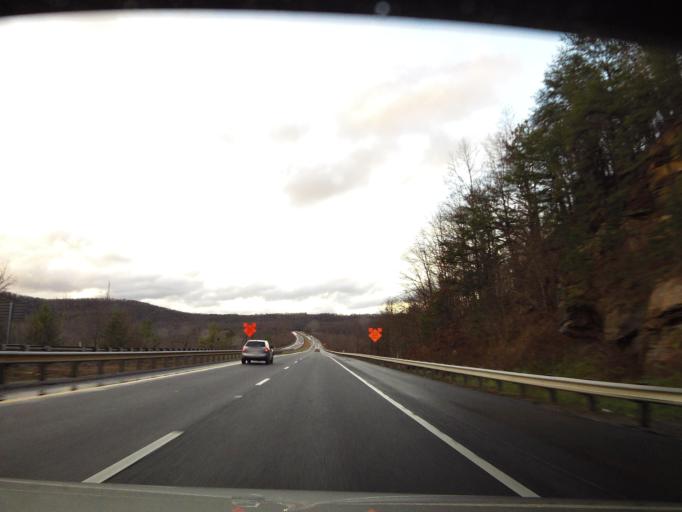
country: US
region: Tennessee
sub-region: Campbell County
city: Jacksboro
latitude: 36.4165
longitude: -84.2824
